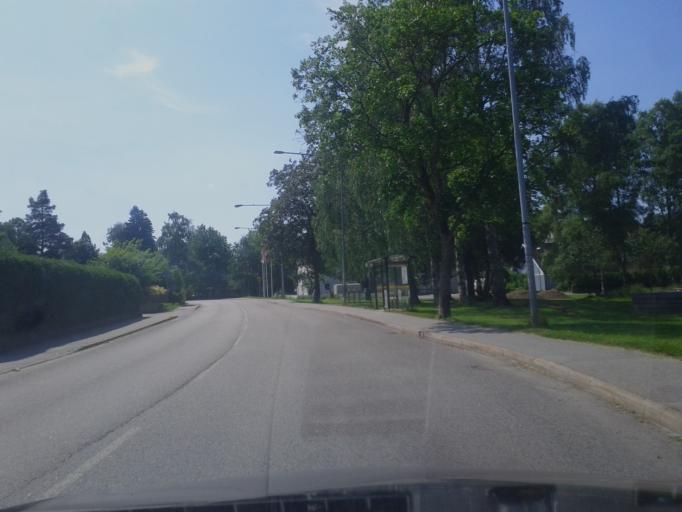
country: SE
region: Stockholm
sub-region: Huddinge Kommun
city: Huddinge
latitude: 59.2489
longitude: 17.9970
